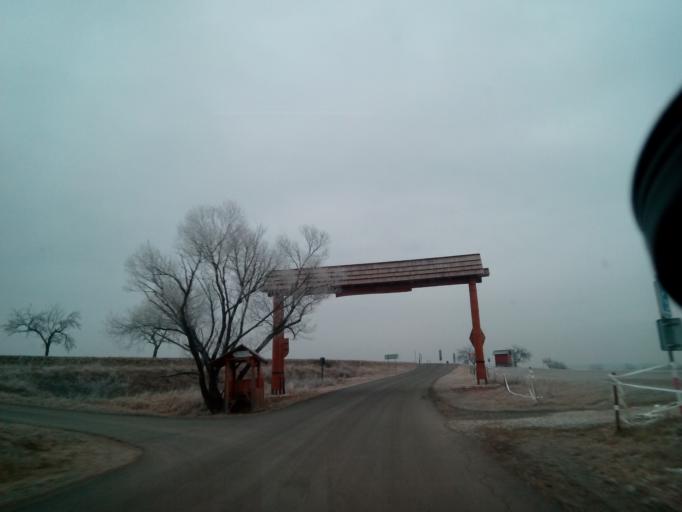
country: SK
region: Presovsky
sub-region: Okres Poprad
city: Poprad
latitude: 48.9674
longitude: 20.3865
